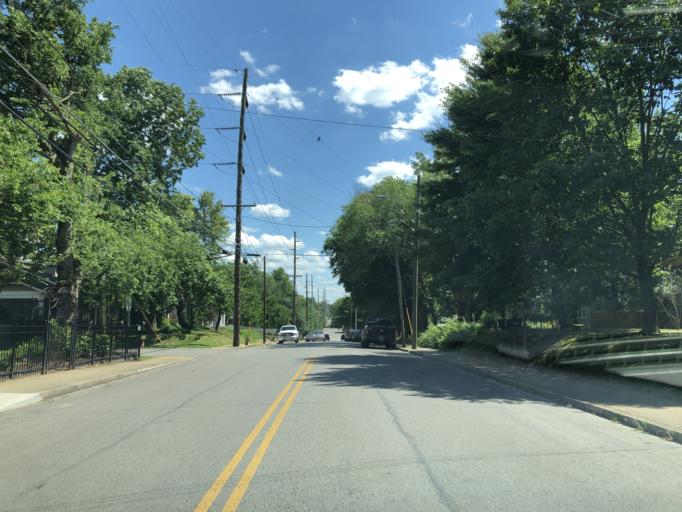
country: US
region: Tennessee
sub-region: Davidson County
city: Nashville
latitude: 36.1816
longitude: -86.7412
